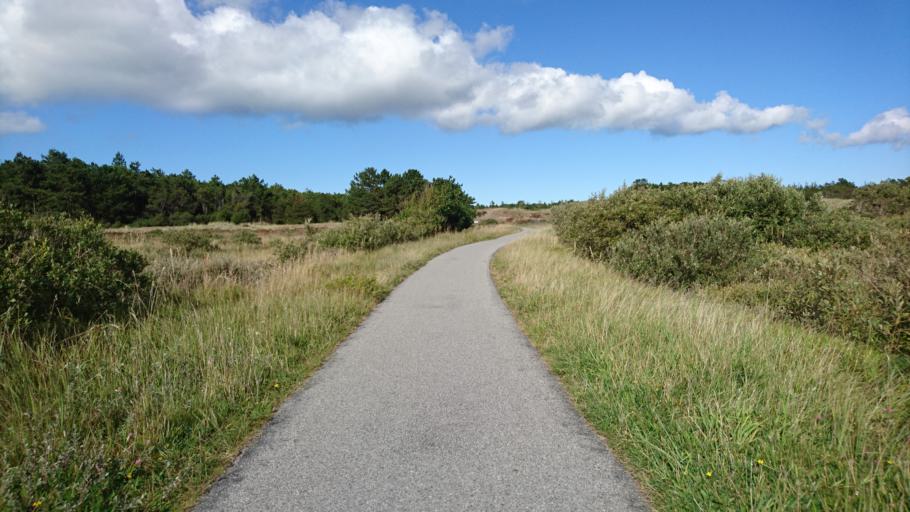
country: DK
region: North Denmark
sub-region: Frederikshavn Kommune
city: Skagen
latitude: 57.6929
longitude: 10.5039
